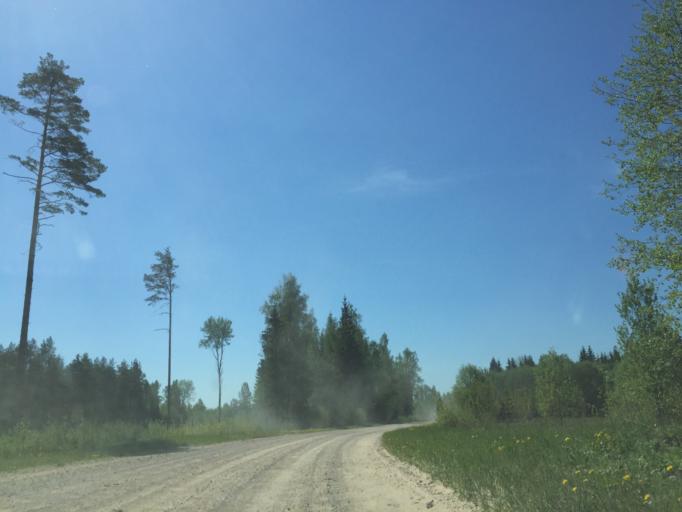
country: LV
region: Kegums
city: Kegums
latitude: 56.8863
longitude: 24.7894
